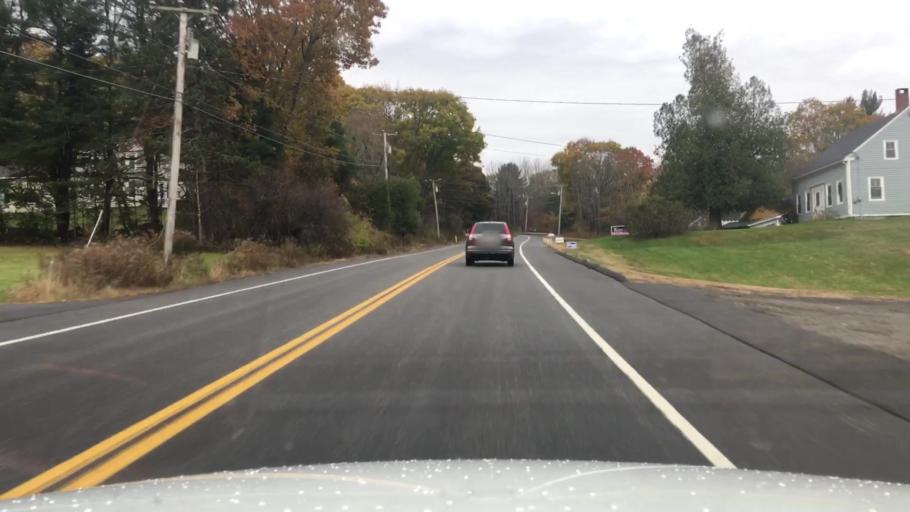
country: US
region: Maine
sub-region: Kennebec County
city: Pittston
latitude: 44.1846
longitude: -69.7461
